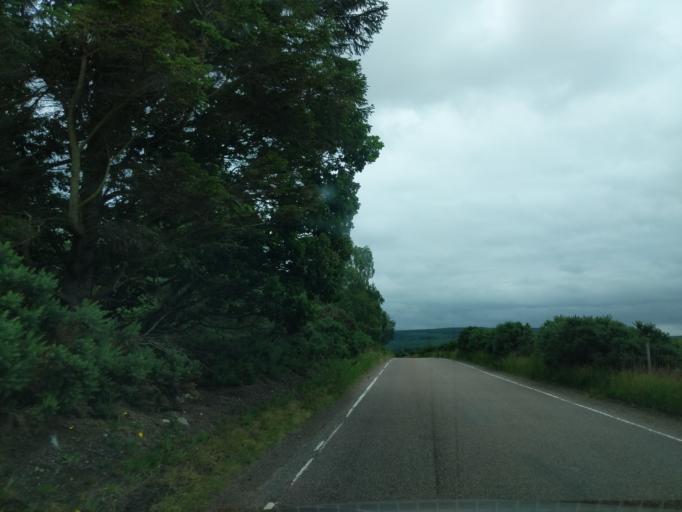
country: GB
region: Scotland
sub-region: Moray
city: Kinloss
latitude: 57.5754
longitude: -3.5495
